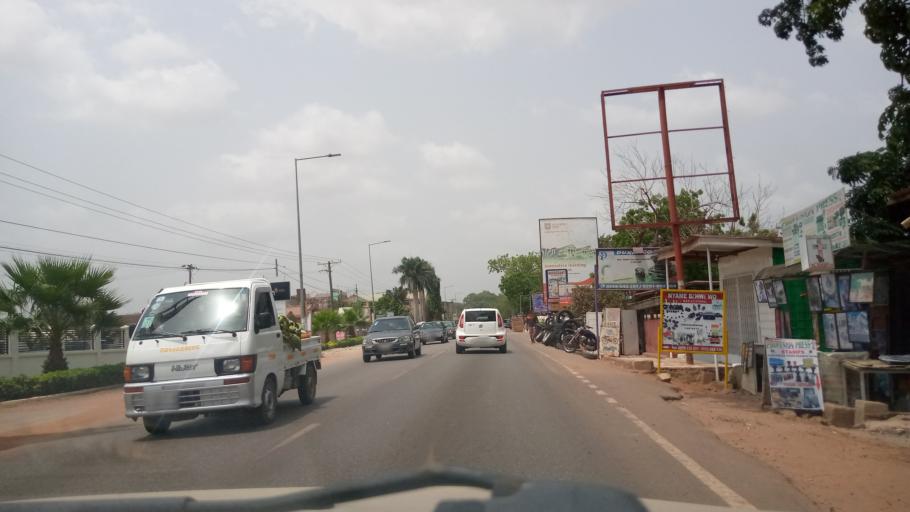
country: GH
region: Greater Accra
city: Dome
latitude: 5.6676
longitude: -0.2141
